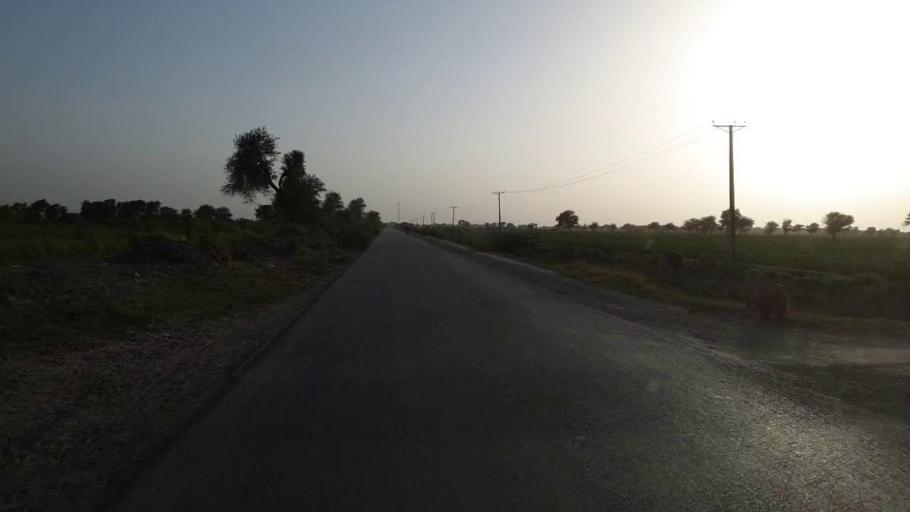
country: PK
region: Sindh
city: Jam Sahib
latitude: 26.2729
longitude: 68.5444
